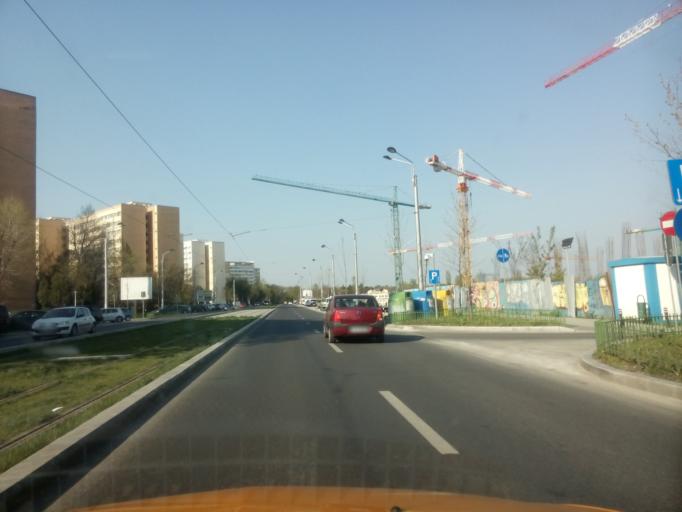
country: RO
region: Ilfov
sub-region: Comuna Popesti-Leordeni
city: Popesti-Leordeni
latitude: 44.4193
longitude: 26.1476
